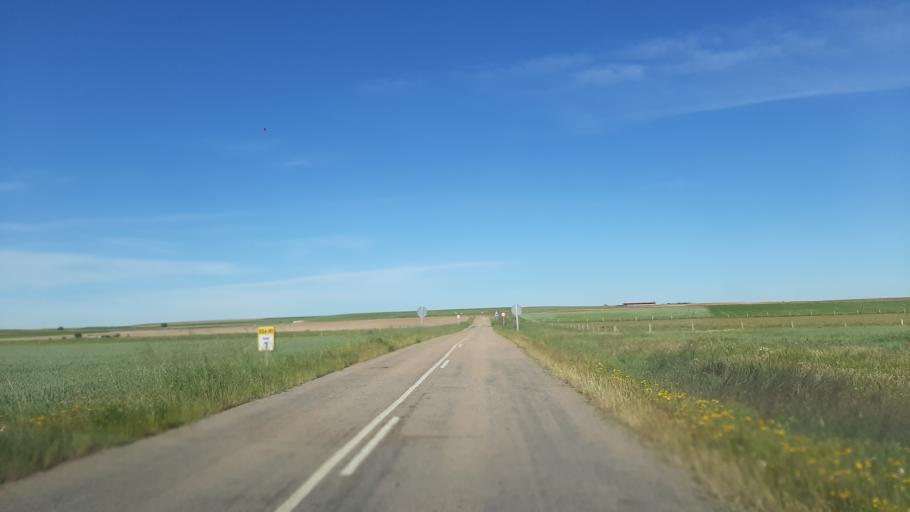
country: ES
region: Castille and Leon
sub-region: Provincia de Salamanca
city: Aldeaseca de Alba
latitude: 40.8258
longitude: -5.4382
